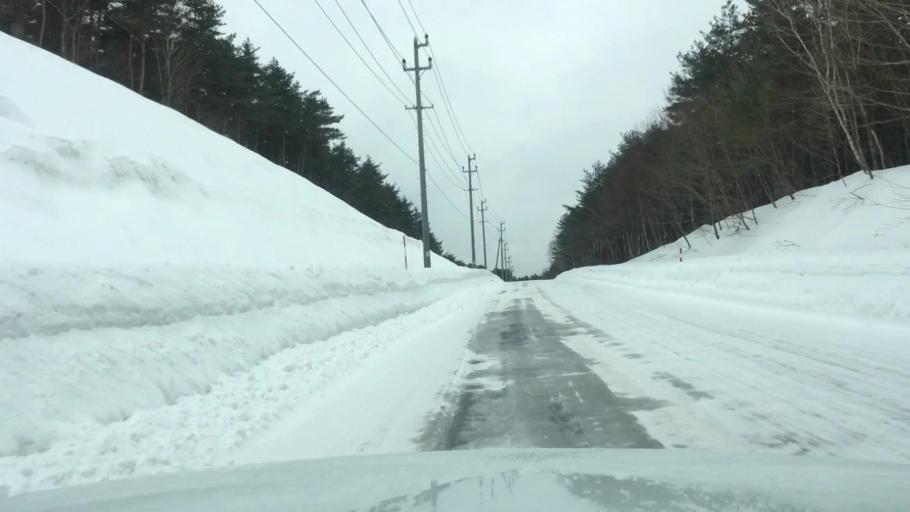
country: JP
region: Iwate
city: Shizukuishi
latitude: 39.9800
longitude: 141.0011
